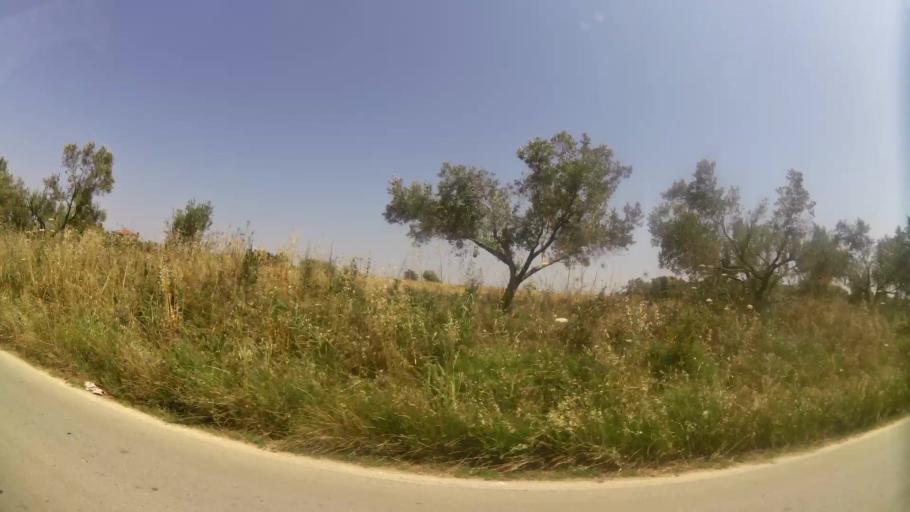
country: GR
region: Central Macedonia
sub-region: Nomos Thessalonikis
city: Nea Michaniona
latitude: 40.4733
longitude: 22.8780
